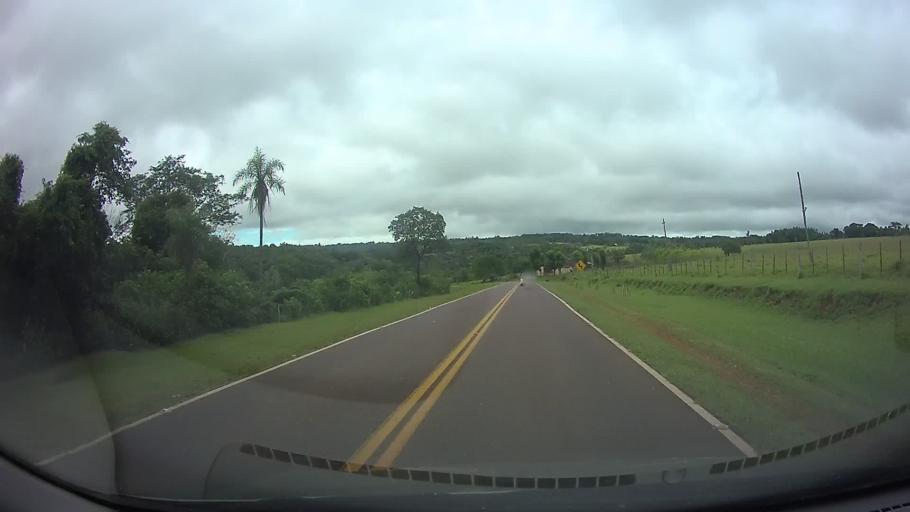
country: PY
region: Paraguari
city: Acahay
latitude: -25.9254
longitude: -57.1075
